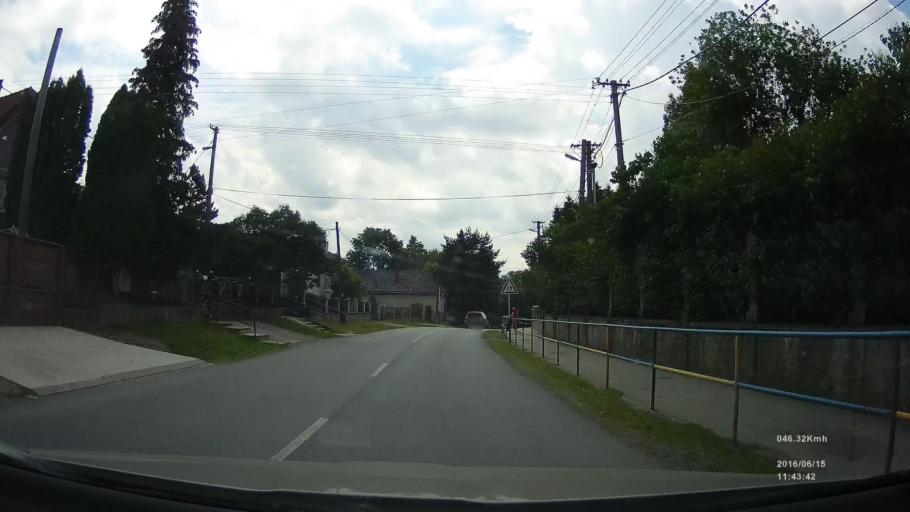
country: SK
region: Kosicky
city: Kosice
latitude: 48.7500
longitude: 21.3446
